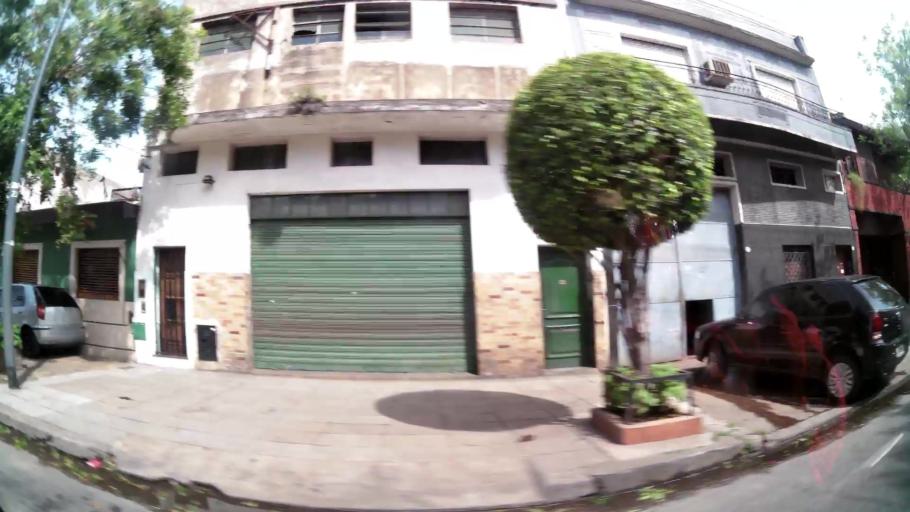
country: AR
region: Buenos Aires F.D.
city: Villa Lugano
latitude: -34.6549
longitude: -58.4344
